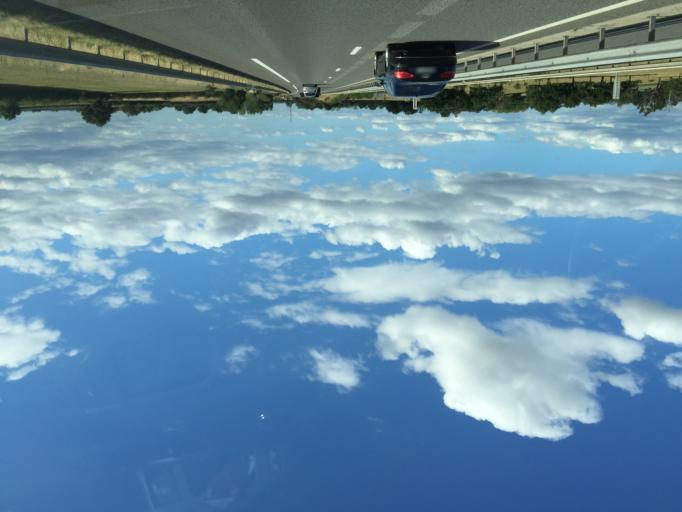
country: FR
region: Rhone-Alpes
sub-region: Departement de la Loire
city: Montrond-les-Bains
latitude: 45.6255
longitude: 4.2007
